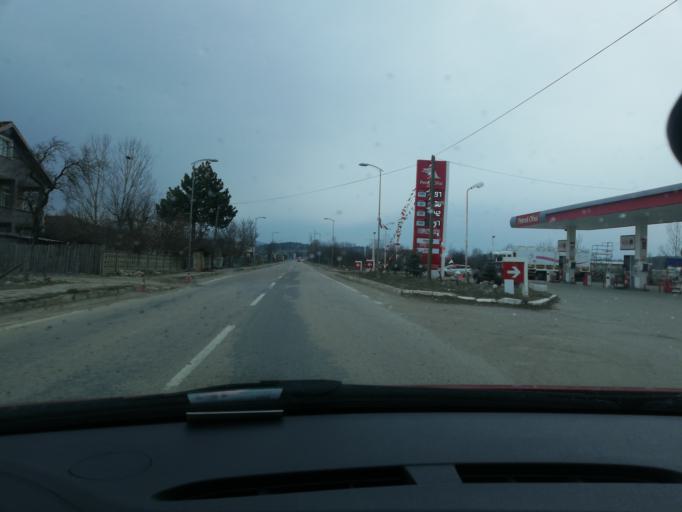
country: TR
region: Kastamonu
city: Daday
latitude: 41.4793
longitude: 33.4767
